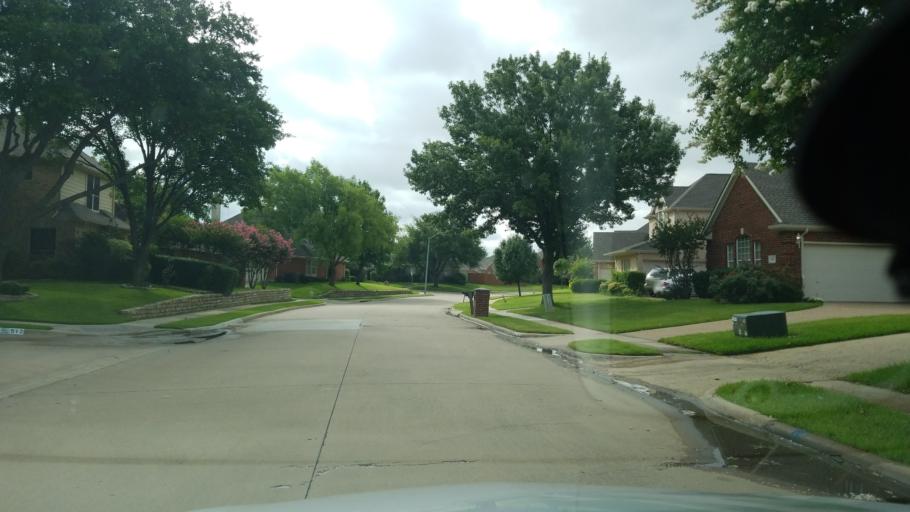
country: US
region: Texas
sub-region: Dallas County
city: Farmers Branch
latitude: 32.9467
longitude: -96.9517
